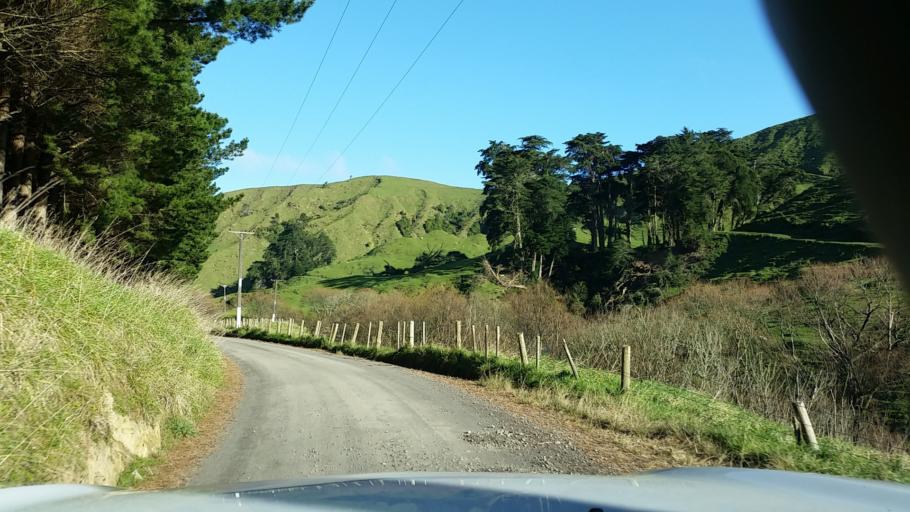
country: NZ
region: Taranaki
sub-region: South Taranaki District
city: Eltham
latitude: -39.5046
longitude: 174.4015
